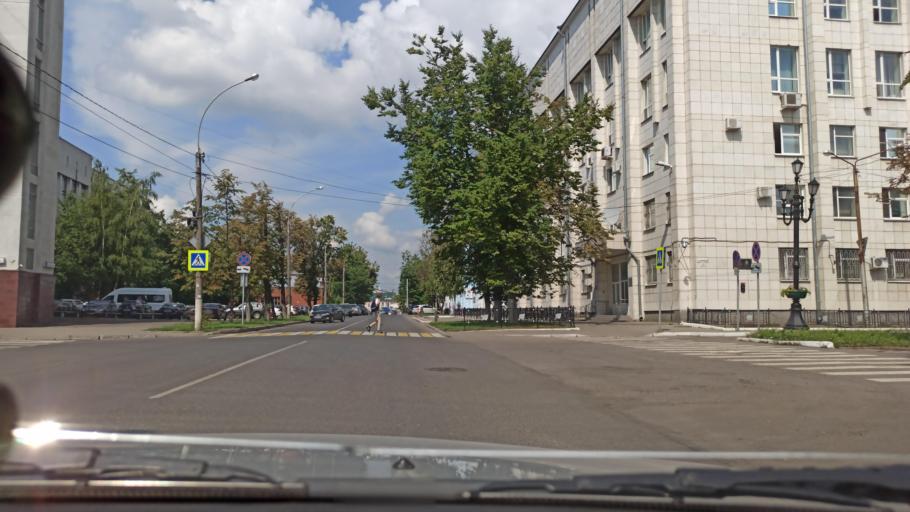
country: RU
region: Vologda
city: Vologda
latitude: 59.2172
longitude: 39.8903
